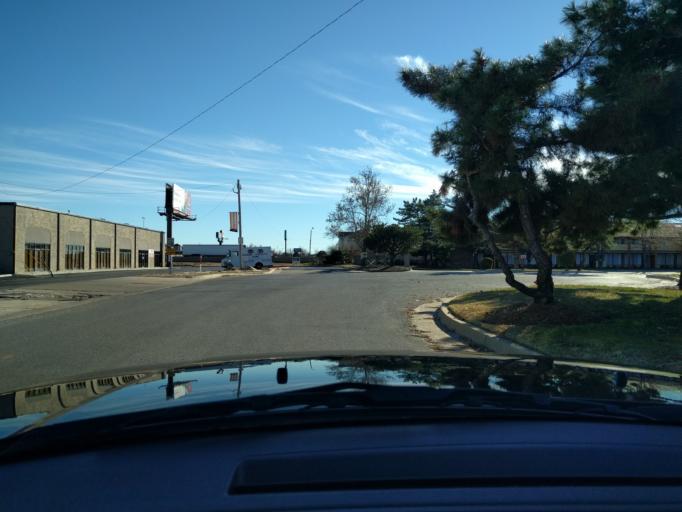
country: US
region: Oklahoma
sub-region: Oklahoma County
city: Warr Acres
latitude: 35.4615
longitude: -97.5971
